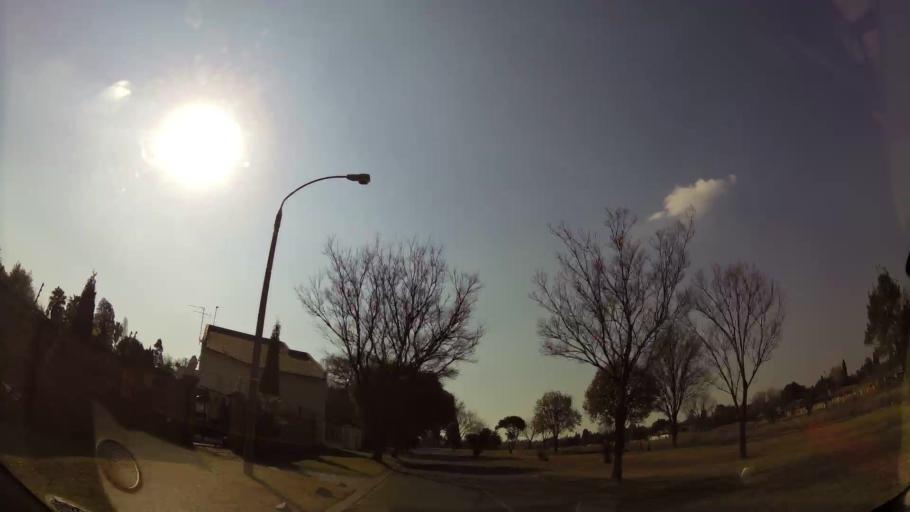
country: ZA
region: Gauteng
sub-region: Ekurhuleni Metropolitan Municipality
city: Benoni
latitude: -26.1537
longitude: 28.2877
